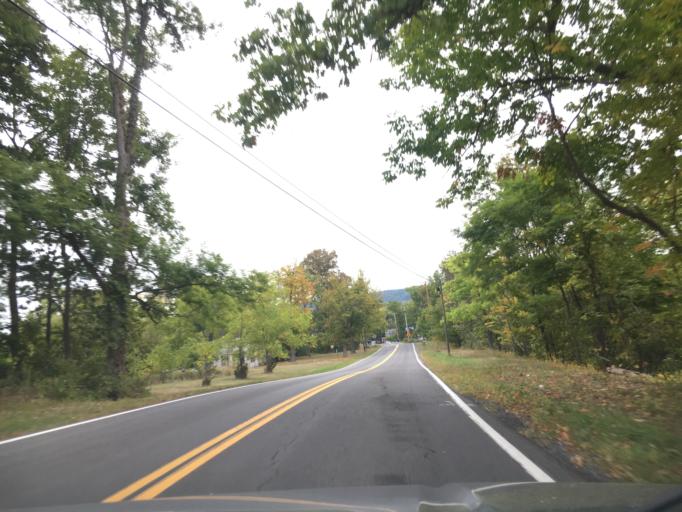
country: US
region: New York
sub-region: Tompkins County
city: Trumansburg
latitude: 42.6634
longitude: -76.7054
